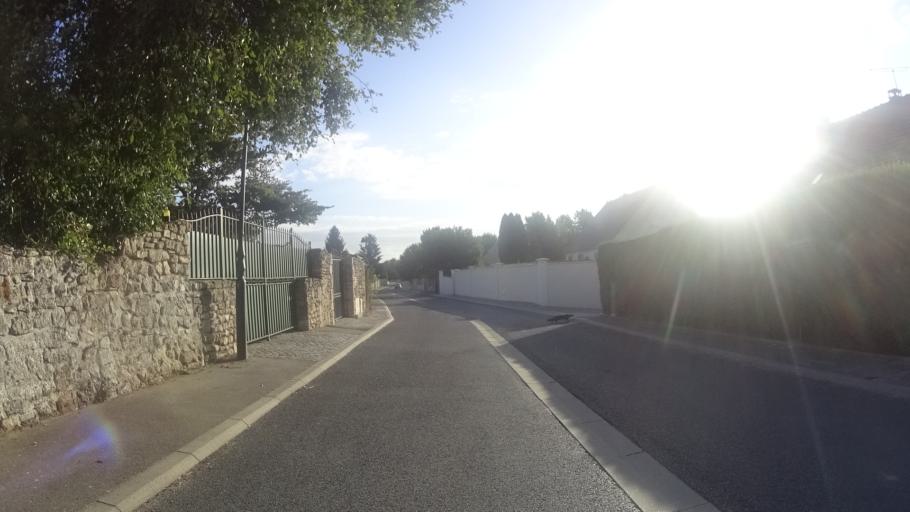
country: FR
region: Picardie
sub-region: Departement de l'Oise
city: Pontpoint
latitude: 49.2741
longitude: 2.6900
